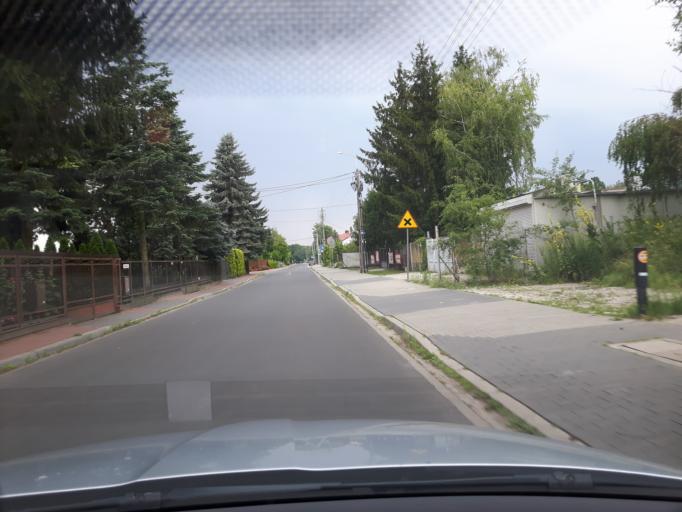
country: PL
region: Masovian Voivodeship
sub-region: Powiat wolominski
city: Zabki
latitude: 52.2943
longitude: 21.1282
